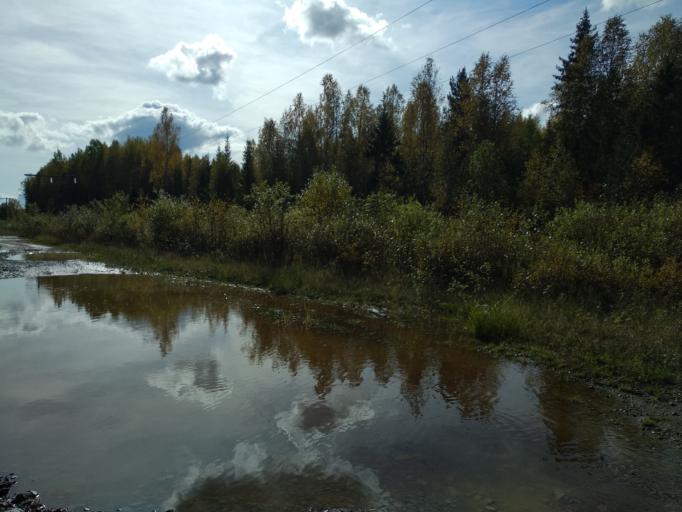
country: RU
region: Sverdlovsk
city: Severoural'sk
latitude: 59.9661
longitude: 59.7944
